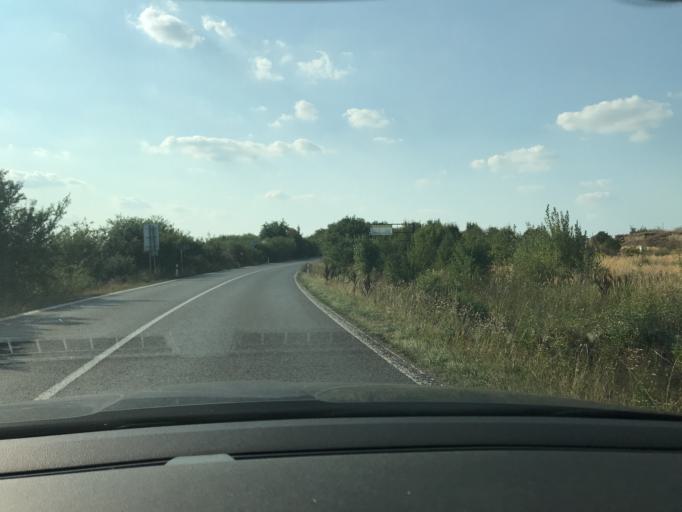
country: CZ
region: Central Bohemia
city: Nelahozeves
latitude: 50.2339
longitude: 14.2691
